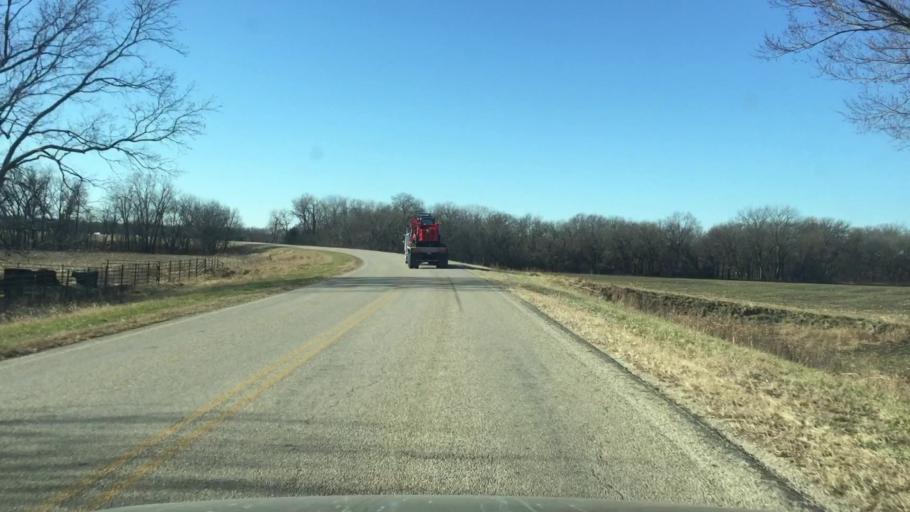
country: US
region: Kansas
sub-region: Allen County
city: Iola
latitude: 37.8845
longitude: -95.4322
